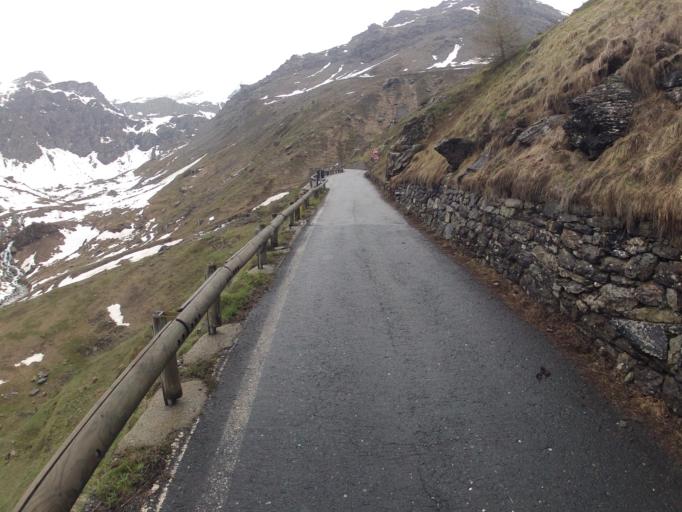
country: IT
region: Piedmont
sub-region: Provincia di Cuneo
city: Crissolo
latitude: 44.7015
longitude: 7.1133
